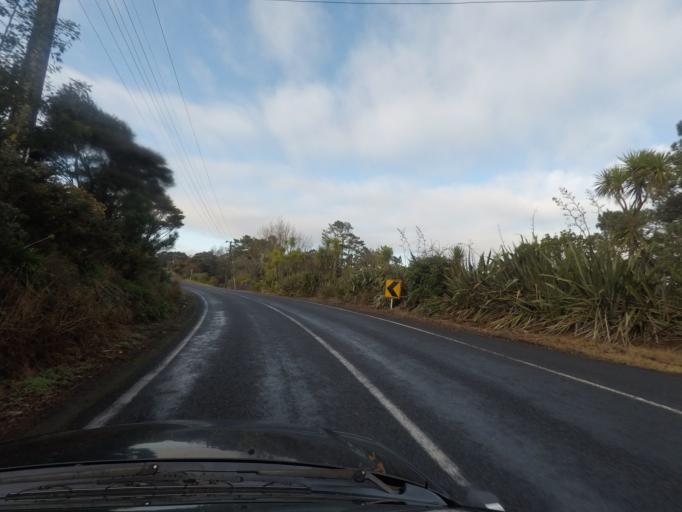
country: NZ
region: Auckland
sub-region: Auckland
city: Waitakere
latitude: -36.9075
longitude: 174.6081
